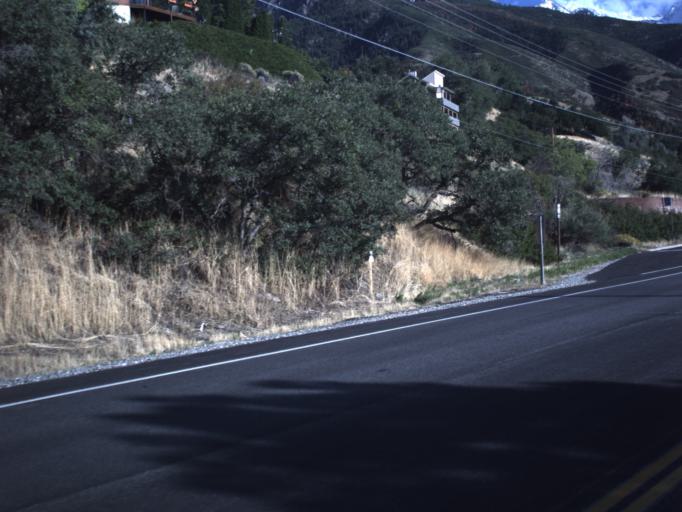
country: US
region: Utah
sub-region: Salt Lake County
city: Granite
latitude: 40.5964
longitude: -111.7973
